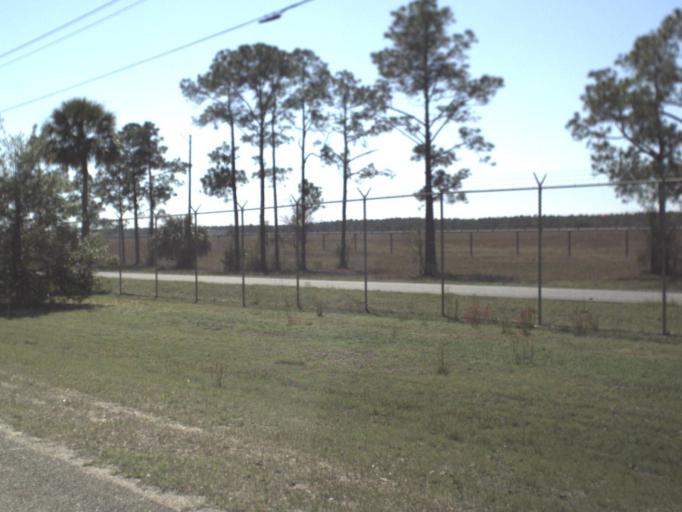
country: US
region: Florida
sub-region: Leon County
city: Tallahassee
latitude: 30.4116
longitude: -84.3530
